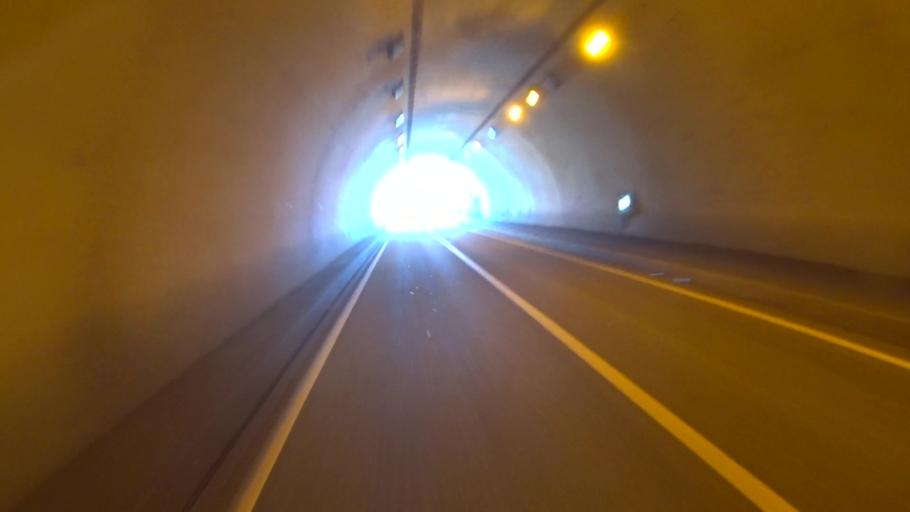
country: JP
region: Kyoto
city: Maizuru
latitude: 35.5125
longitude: 135.3798
